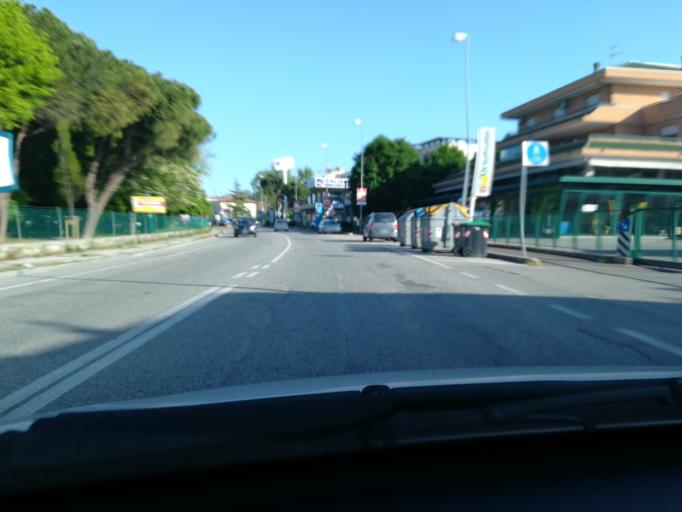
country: IT
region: Emilia-Romagna
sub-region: Provincia di Rimini
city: Riccione
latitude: 43.9943
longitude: 12.6492
